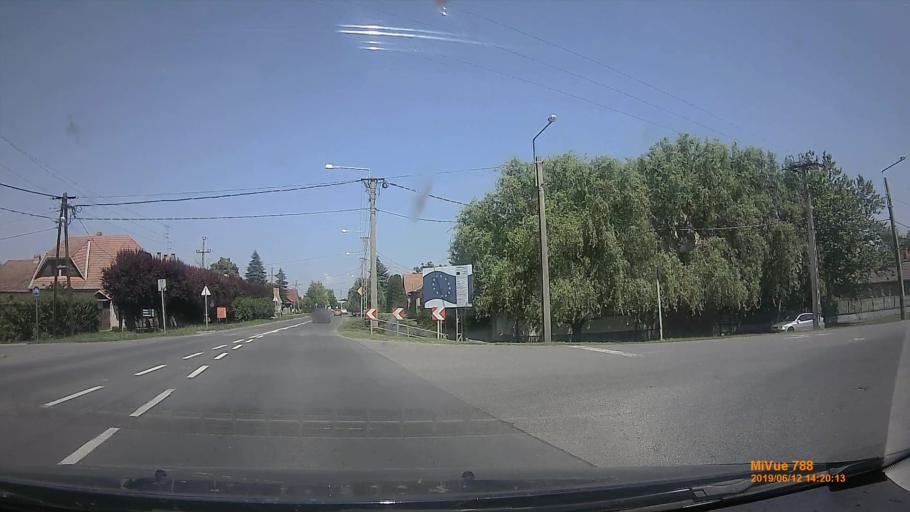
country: HU
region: Csongrad
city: Deszk
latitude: 46.2200
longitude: 20.2435
